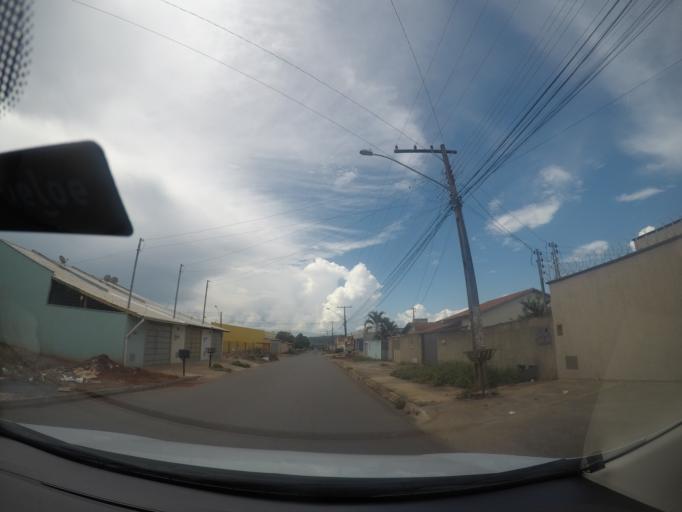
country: BR
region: Goias
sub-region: Goiania
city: Goiania
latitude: -16.7013
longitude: -49.3567
